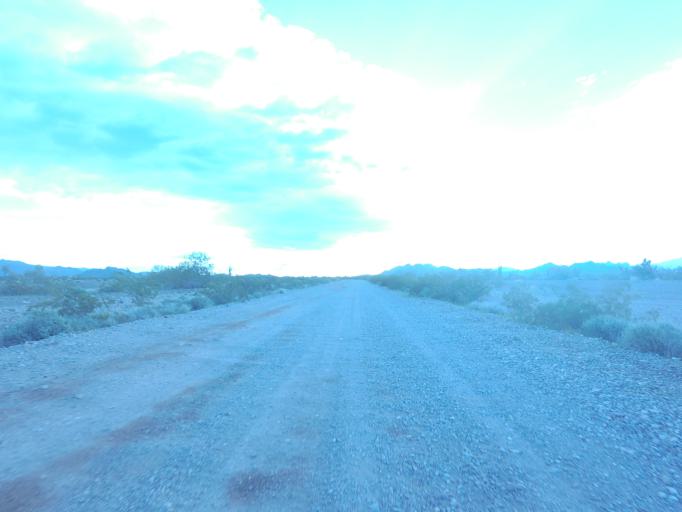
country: US
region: Arizona
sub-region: La Paz County
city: Quartzsite
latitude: 33.5335
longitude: -114.1966
